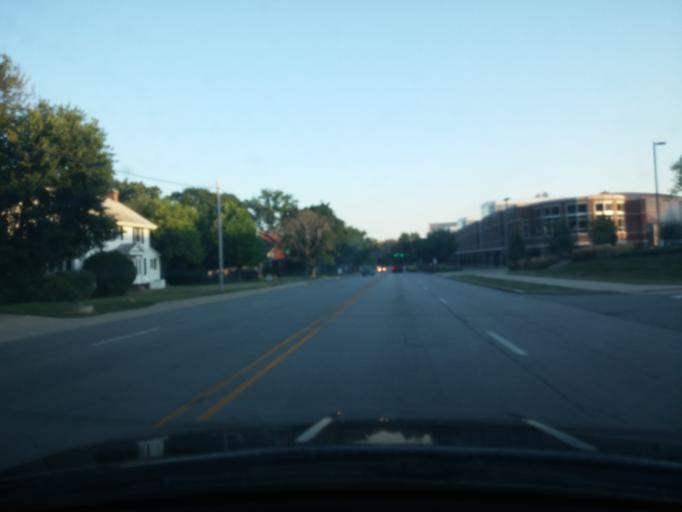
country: US
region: Indiana
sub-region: Tippecanoe County
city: West Lafayette
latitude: 40.4356
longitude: -86.9154
